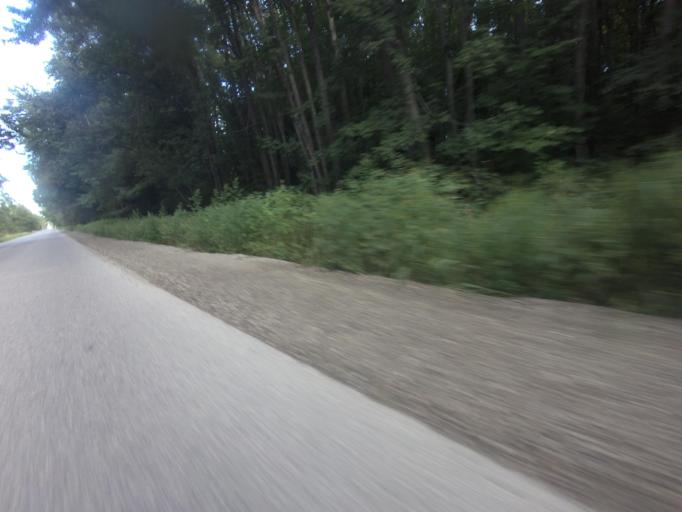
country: CA
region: Ontario
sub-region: Wellington County
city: Guelph
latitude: 43.6053
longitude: -80.3531
